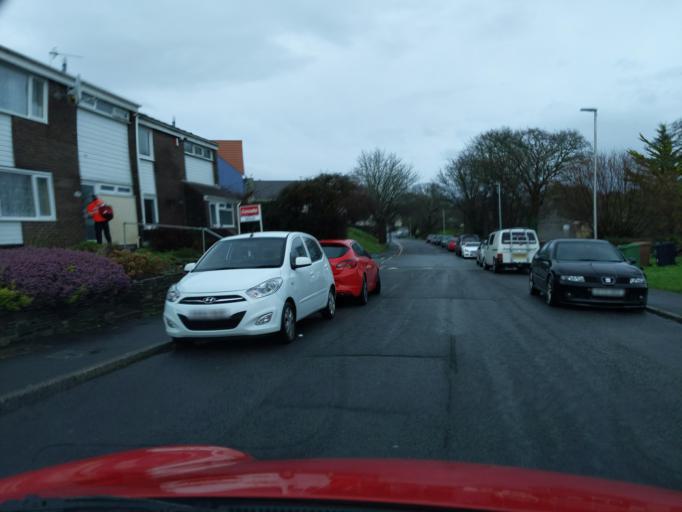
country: GB
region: England
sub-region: Plymouth
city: Plymouth
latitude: 50.4054
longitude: -4.1534
